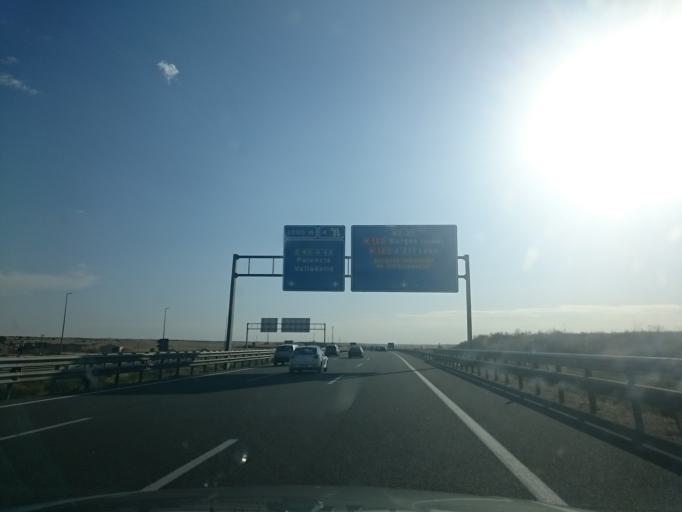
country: ES
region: Castille and Leon
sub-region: Provincia de Burgos
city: Villagonzalo-Pedernales
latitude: 42.3073
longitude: -3.7346
